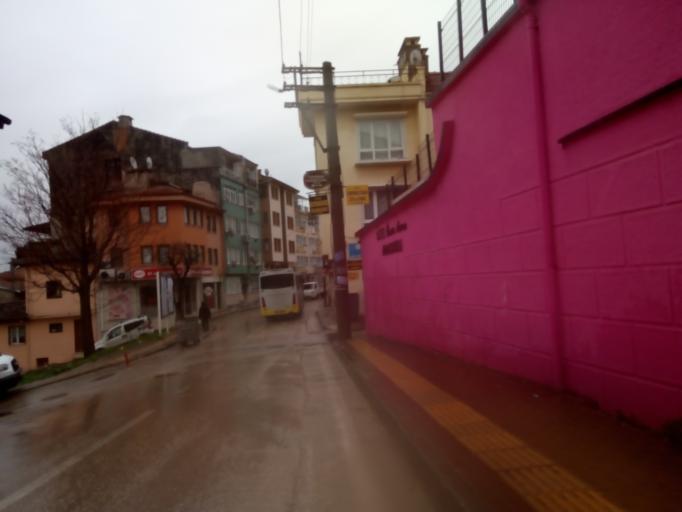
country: TR
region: Bursa
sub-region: Osmangazi
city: Bursa
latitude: 40.1796
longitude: 29.0581
